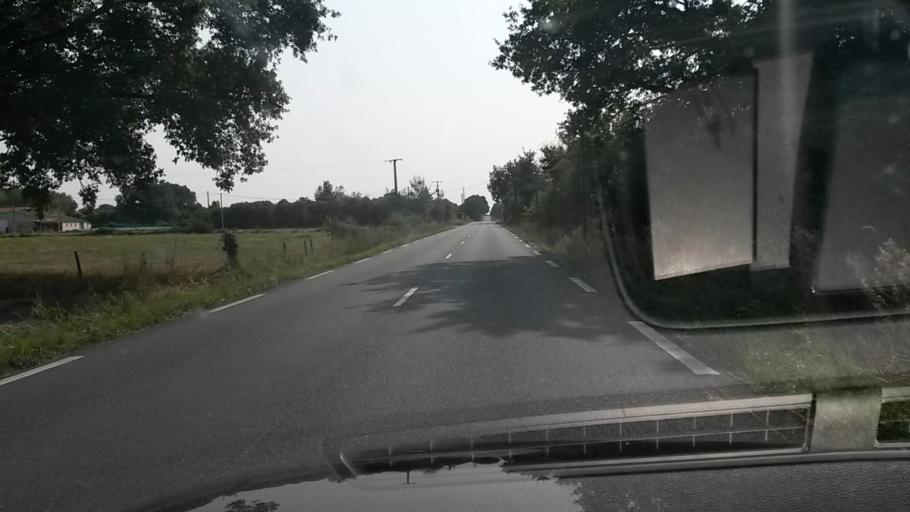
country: FR
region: Pays de la Loire
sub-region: Departement de la Loire-Atlantique
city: La Remaudiere
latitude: 47.2031
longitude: -1.2447
